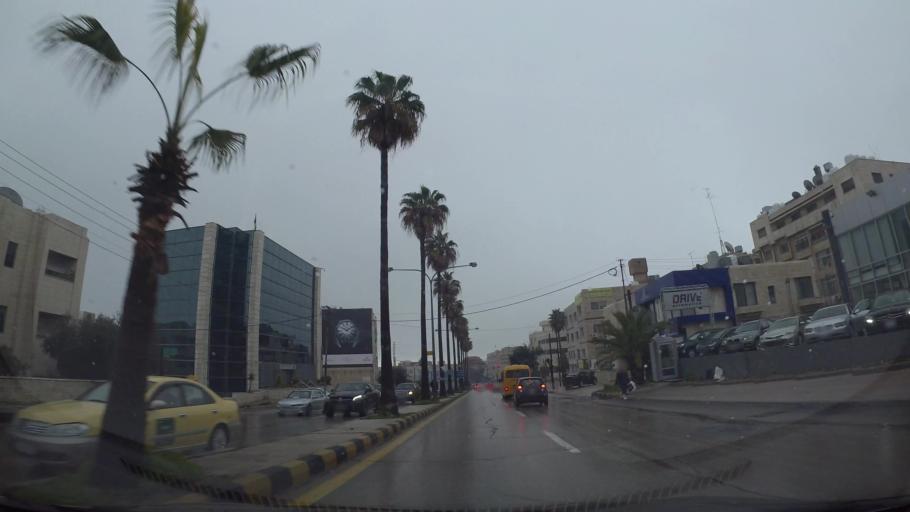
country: JO
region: Amman
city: Amman
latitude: 31.9653
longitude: 35.8829
